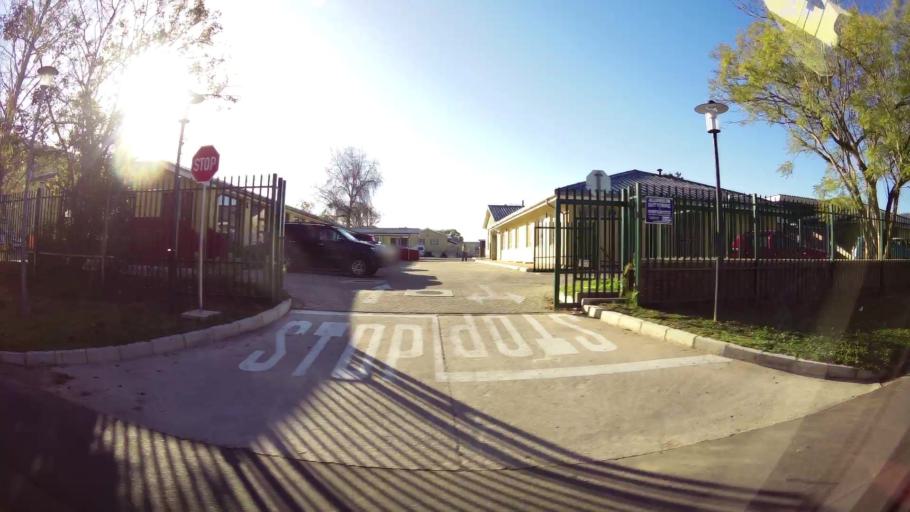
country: ZA
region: Western Cape
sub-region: Eden District Municipality
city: George
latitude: -33.9482
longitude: 22.4511
